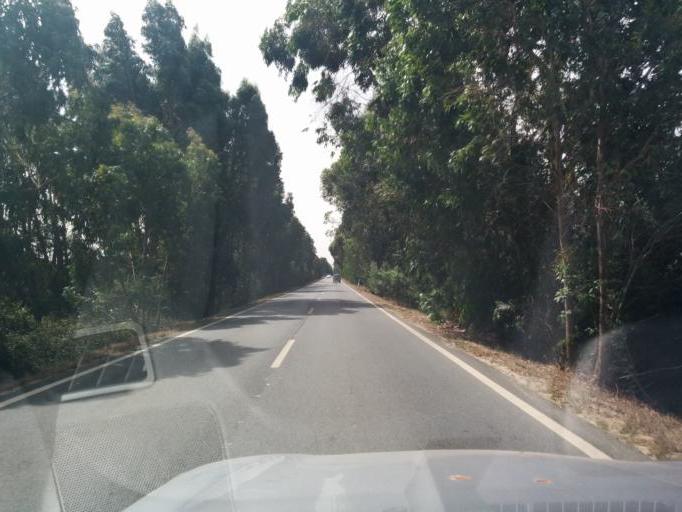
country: PT
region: Beja
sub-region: Odemira
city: Vila Nova de Milfontes
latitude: 37.6847
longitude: -8.7646
